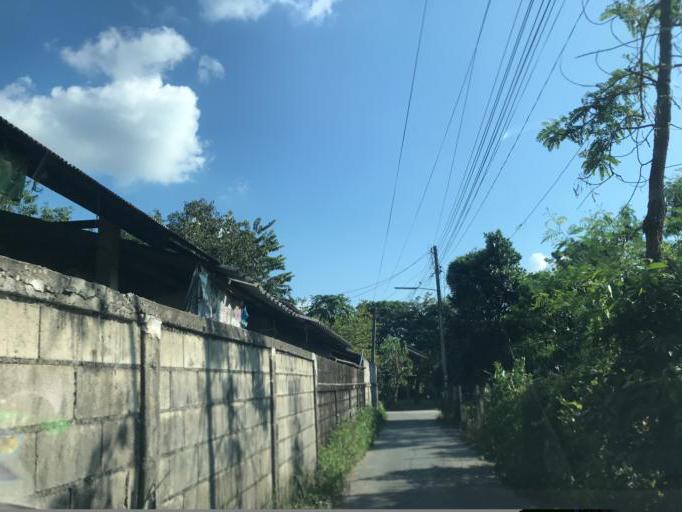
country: TH
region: Chiang Mai
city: San Pa Tong
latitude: 18.6543
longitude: 98.8635
